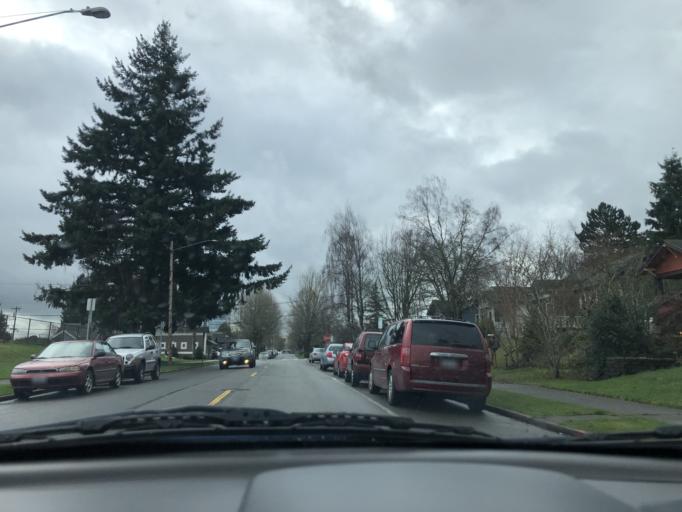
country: US
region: Washington
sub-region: Snohomish County
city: Everett
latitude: 48.0051
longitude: -122.2066
